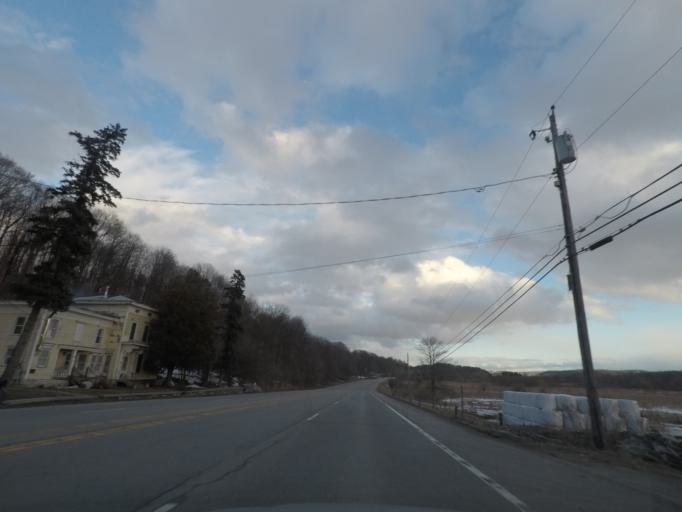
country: US
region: New York
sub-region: Herkimer County
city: Little Falls
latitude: 43.0323
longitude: -74.8022
